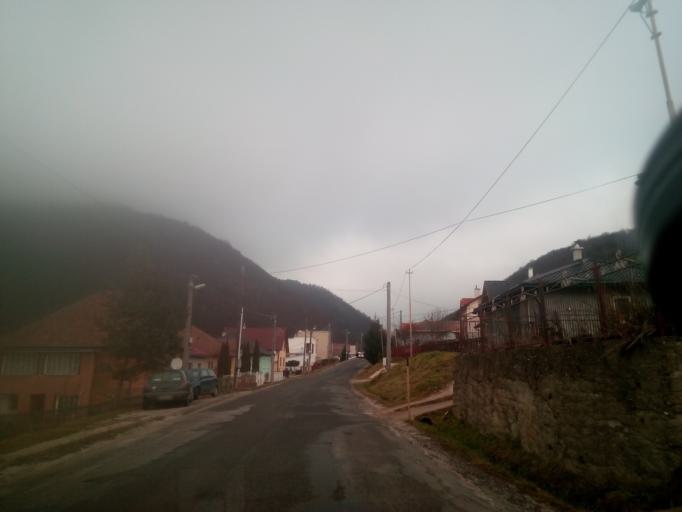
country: SK
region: Kosicky
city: Krompachy
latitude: 48.9369
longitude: 20.9411
